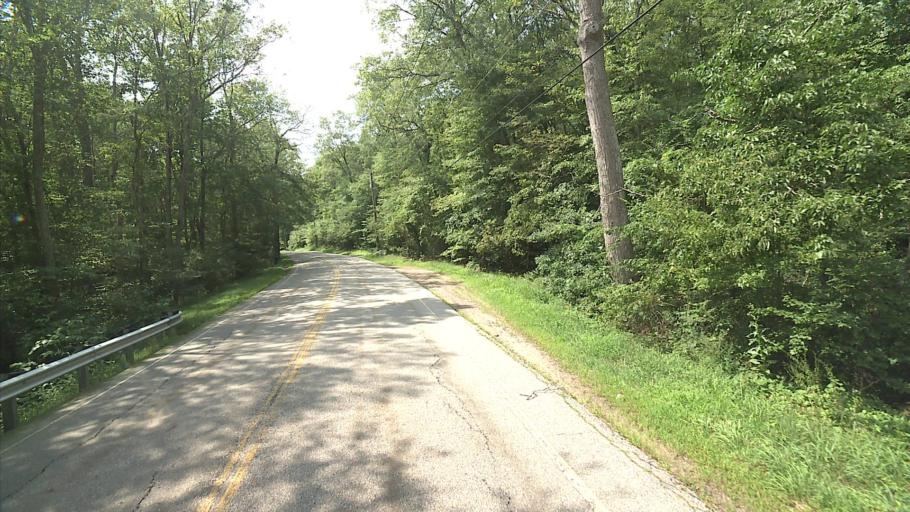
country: US
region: Connecticut
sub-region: Middlesex County
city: Essex Village
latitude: 41.4289
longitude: -72.3658
